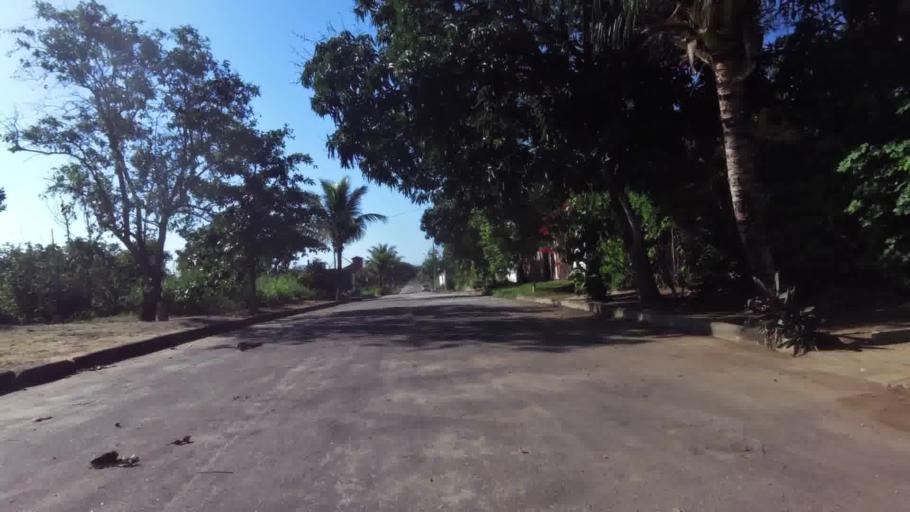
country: BR
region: Espirito Santo
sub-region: Guarapari
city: Guarapari
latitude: -20.7458
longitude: -40.5598
